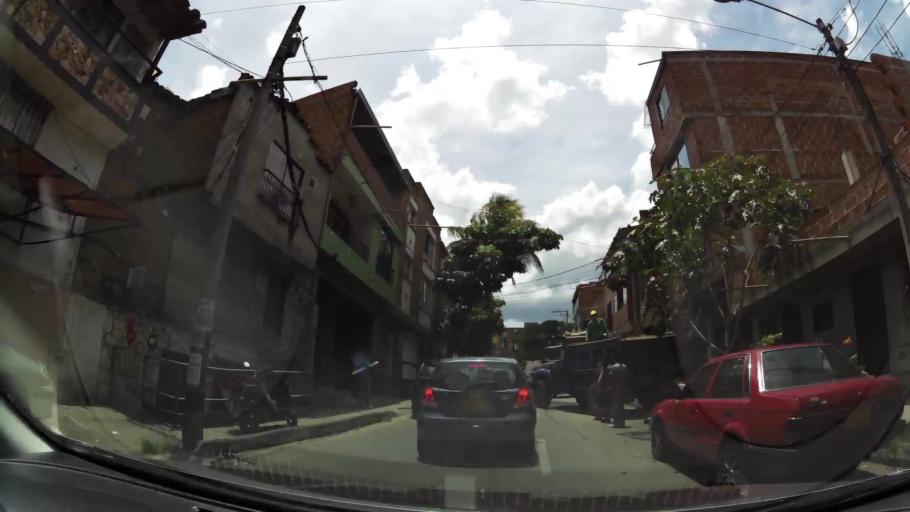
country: CO
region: Antioquia
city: Bello
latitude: 6.3391
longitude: -75.5622
